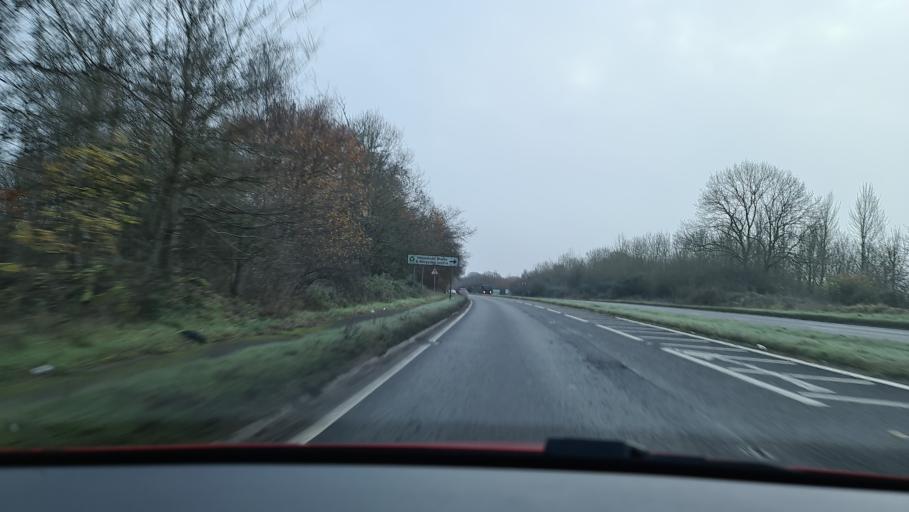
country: GB
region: England
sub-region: Buckinghamshire
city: Seer Green
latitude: 51.5992
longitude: -0.6183
